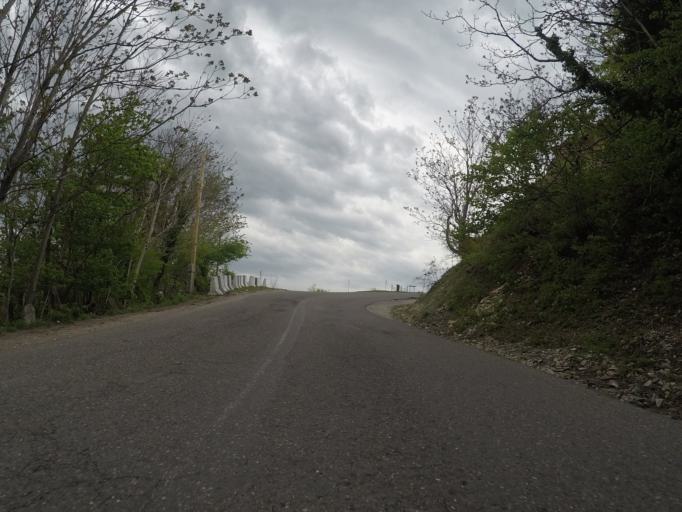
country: GE
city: Tqibuli
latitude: 42.2778
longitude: 43.2043
